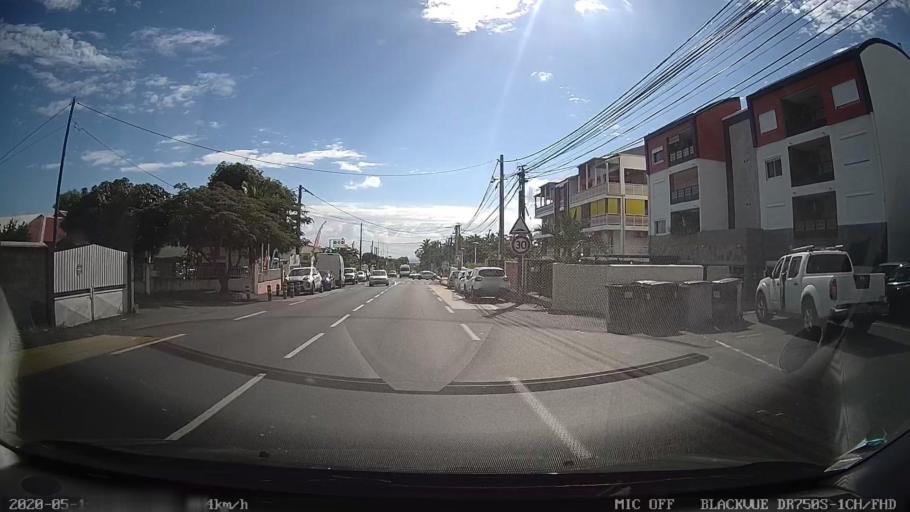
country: RE
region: Reunion
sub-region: Reunion
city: La Possession
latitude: -20.9557
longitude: 55.3235
